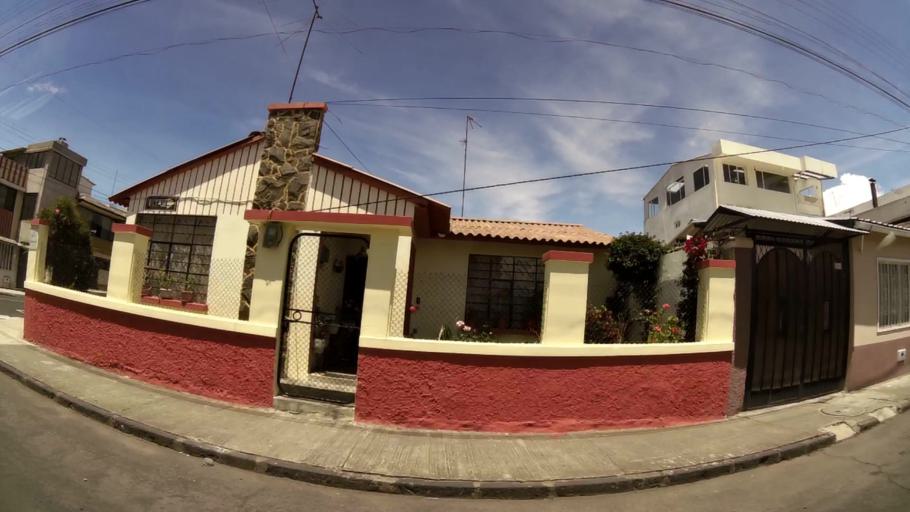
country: EC
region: Chimborazo
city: Riobamba
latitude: -1.6637
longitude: -78.6520
